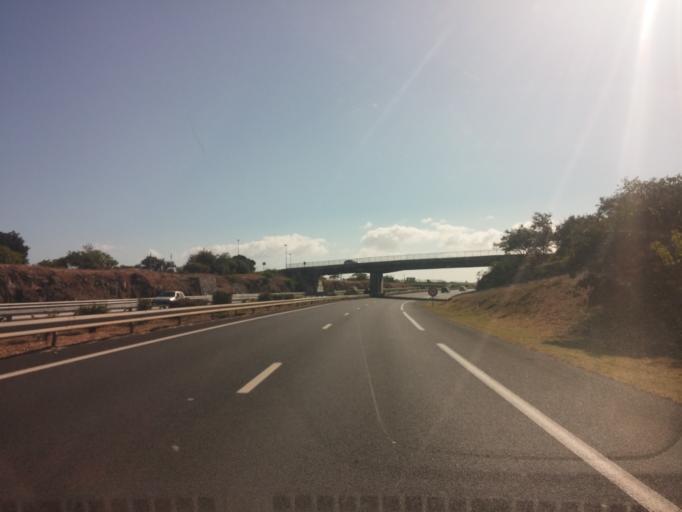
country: RE
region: Reunion
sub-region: Reunion
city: La Possession
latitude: -20.9322
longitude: 55.3311
